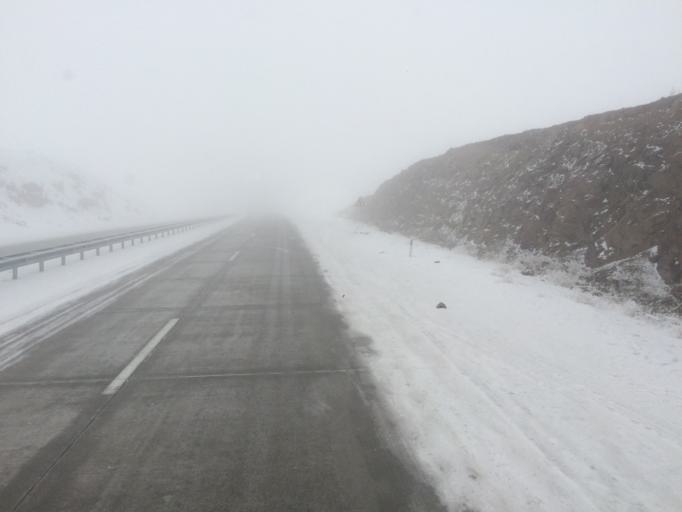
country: KZ
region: Zhambyl
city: Georgiyevka
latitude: 43.4271
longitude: 74.9588
